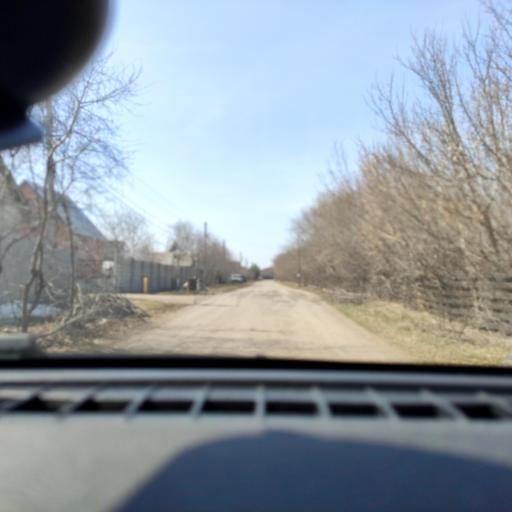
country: RU
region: Samara
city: Podstepki
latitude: 53.5207
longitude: 49.1021
